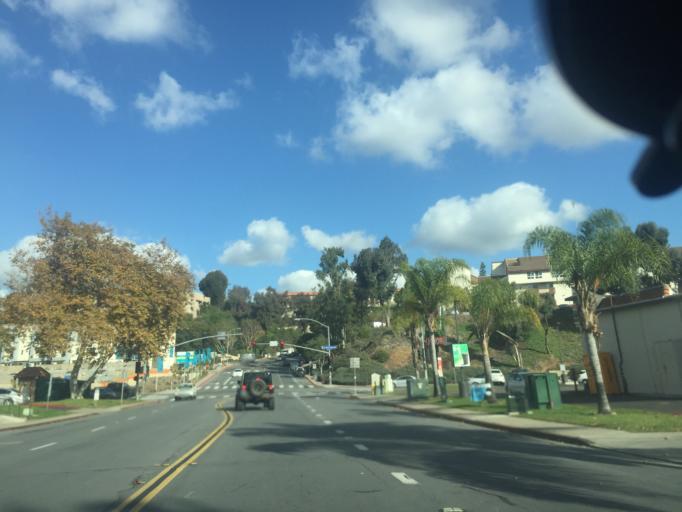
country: US
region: California
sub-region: San Diego County
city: San Diego
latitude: 32.7841
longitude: -117.1104
